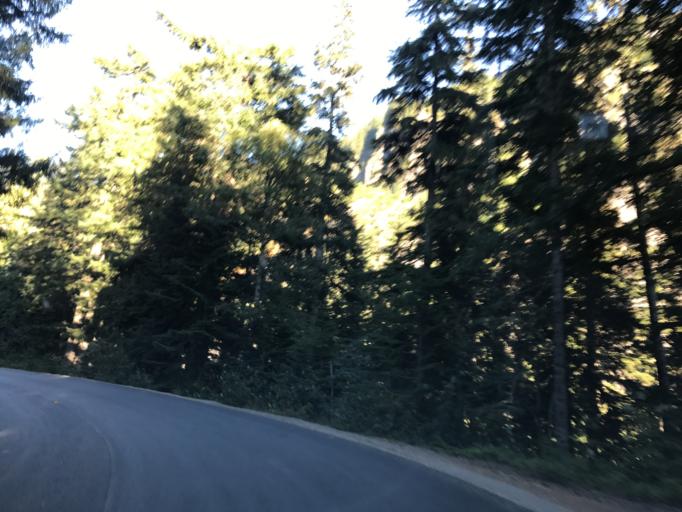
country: US
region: Washington
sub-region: Pierce County
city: Buckley
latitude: 46.7741
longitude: -121.7845
